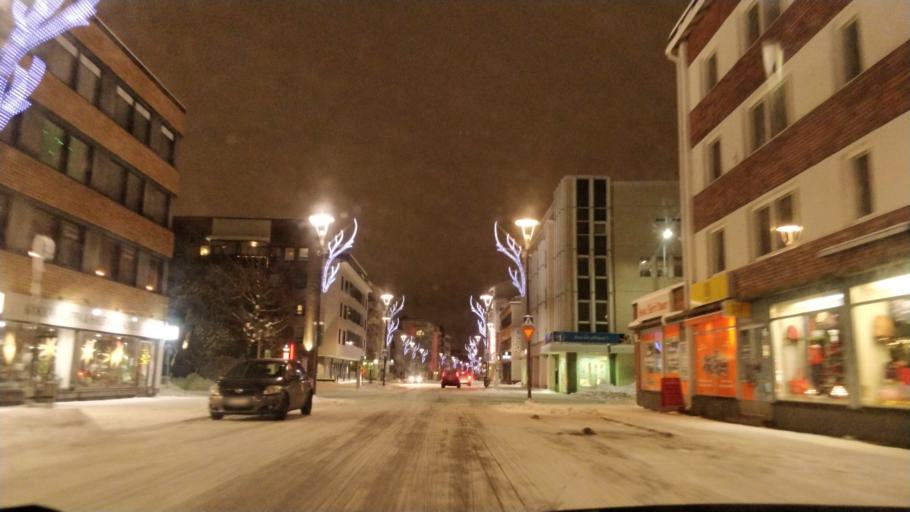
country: FI
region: Lapland
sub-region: Rovaniemi
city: Rovaniemi
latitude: 66.5007
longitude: 25.7271
